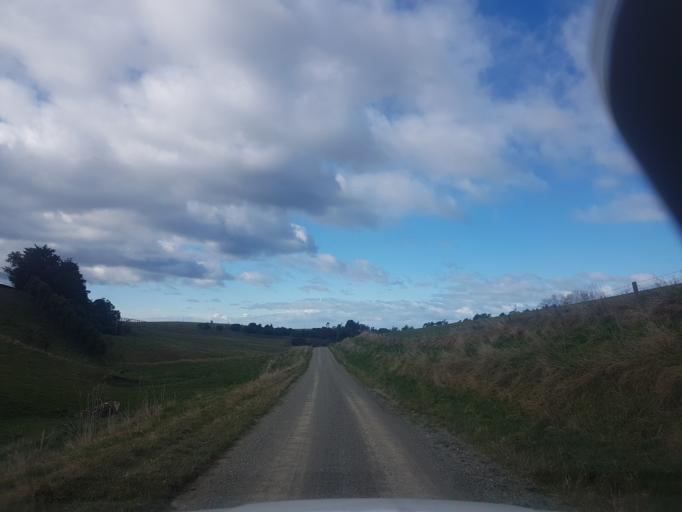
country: NZ
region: Canterbury
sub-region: Timaru District
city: Pleasant Point
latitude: -44.1839
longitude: 171.1347
